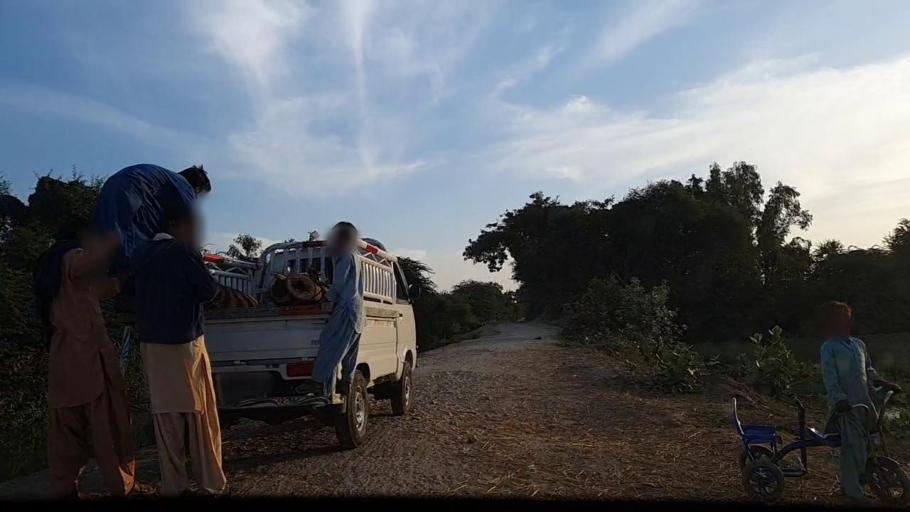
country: PK
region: Sindh
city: Mirpur Batoro
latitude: 24.6383
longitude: 68.1372
